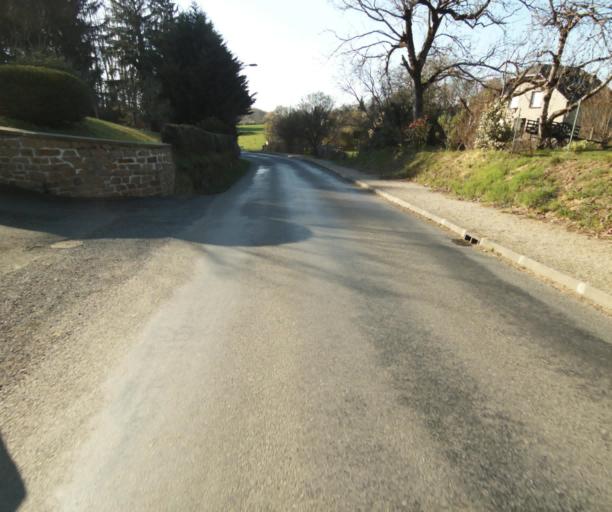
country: FR
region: Limousin
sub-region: Departement de la Correze
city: Saint-Clement
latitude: 45.3416
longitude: 1.6821
